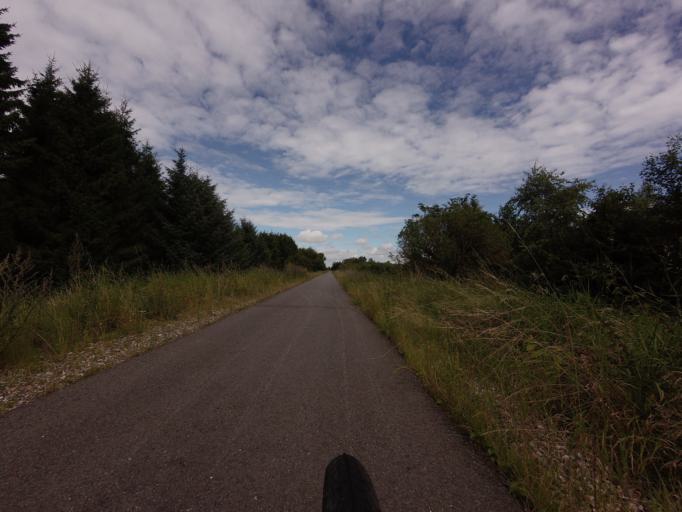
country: DK
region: Central Jutland
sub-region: Norddjurs Kommune
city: Auning
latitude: 56.4145
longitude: 10.3907
